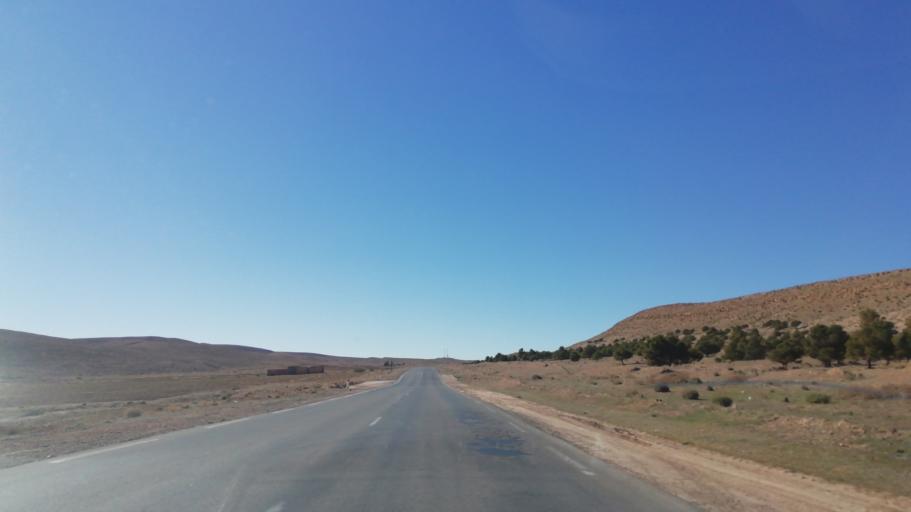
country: DZ
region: El Bayadh
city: El Bayadh
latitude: 33.6800
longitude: 1.4524
